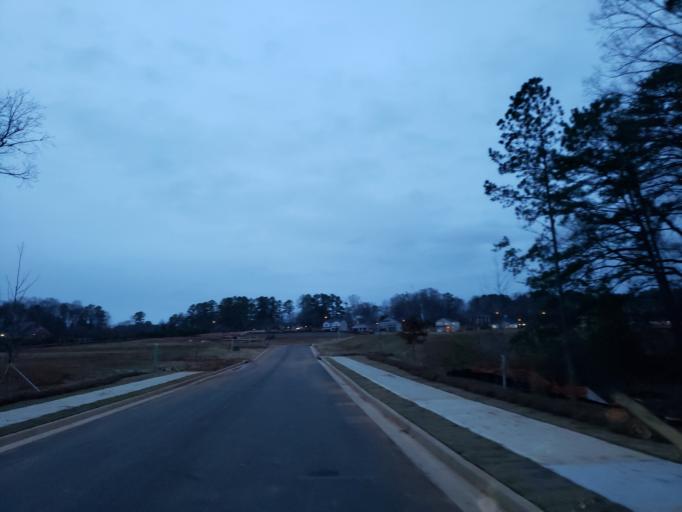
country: US
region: Georgia
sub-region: Cobb County
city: Mableton
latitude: 33.8369
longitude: -84.5810
